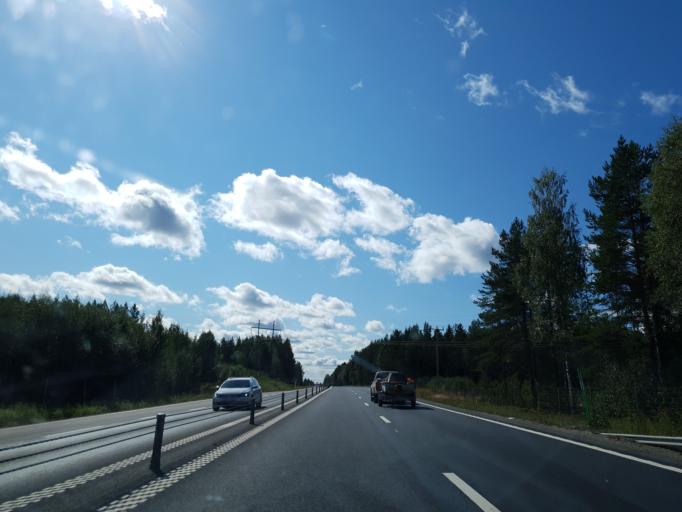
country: SE
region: Vaesterbotten
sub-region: Nordmalings Kommun
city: Nordmaling
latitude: 63.5470
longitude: 19.4116
